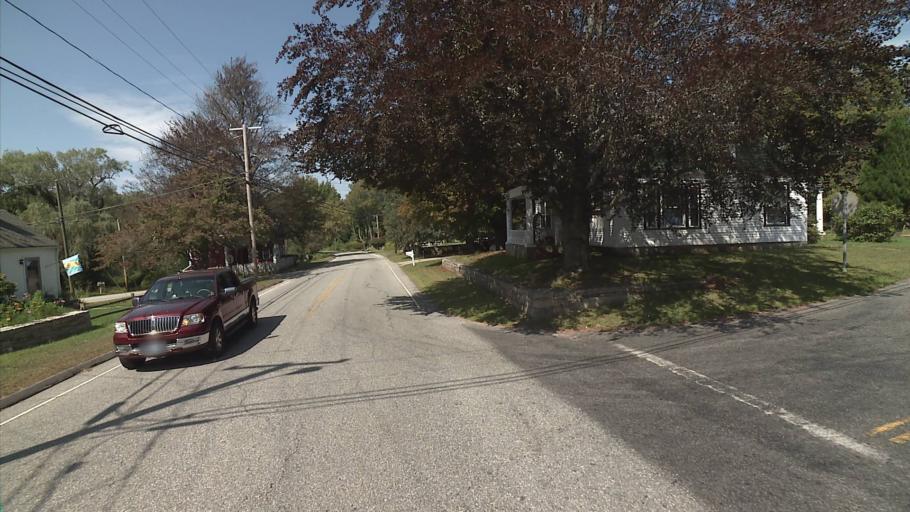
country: US
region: Connecticut
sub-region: Windham County
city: Willimantic
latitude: 41.6659
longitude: -72.2551
